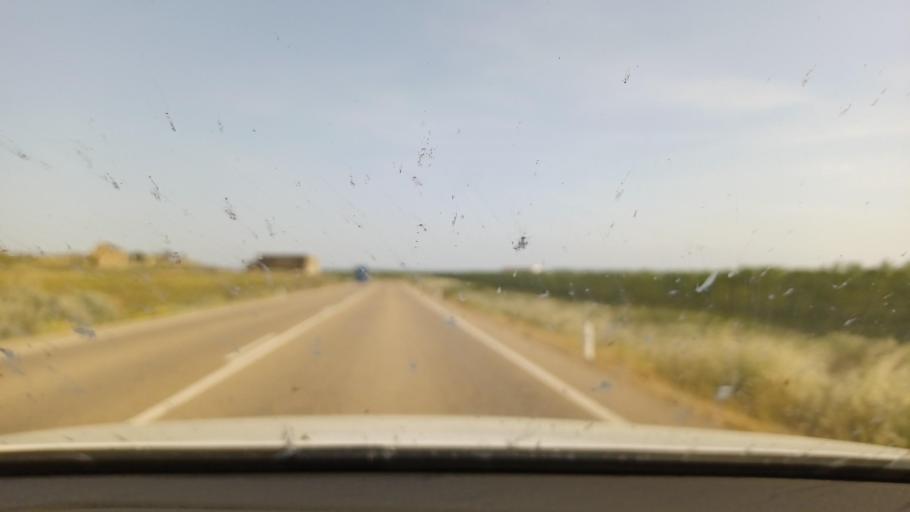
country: ES
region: Aragon
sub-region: Provincia de Zaragoza
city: Chiprana
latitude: 41.3107
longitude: -0.0748
